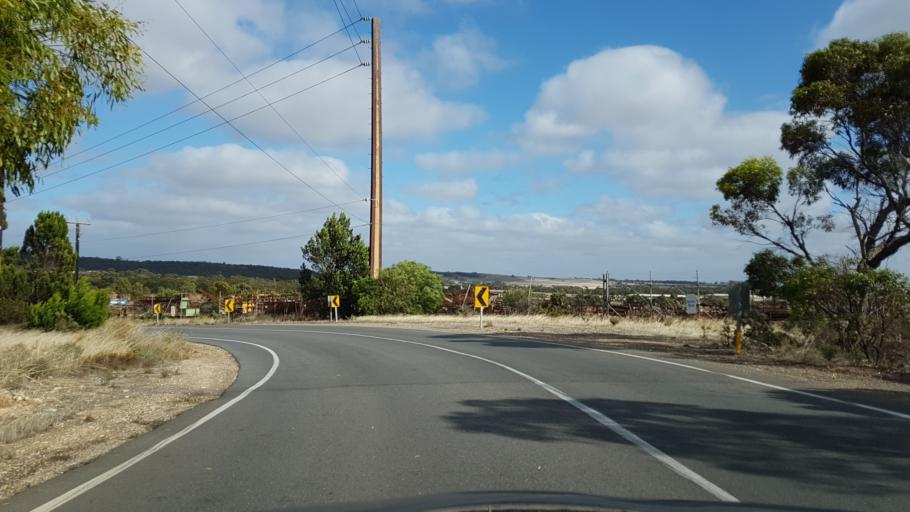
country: AU
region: South Australia
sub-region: Murray Bridge
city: Murray Bridge
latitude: -35.1169
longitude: 139.2464
